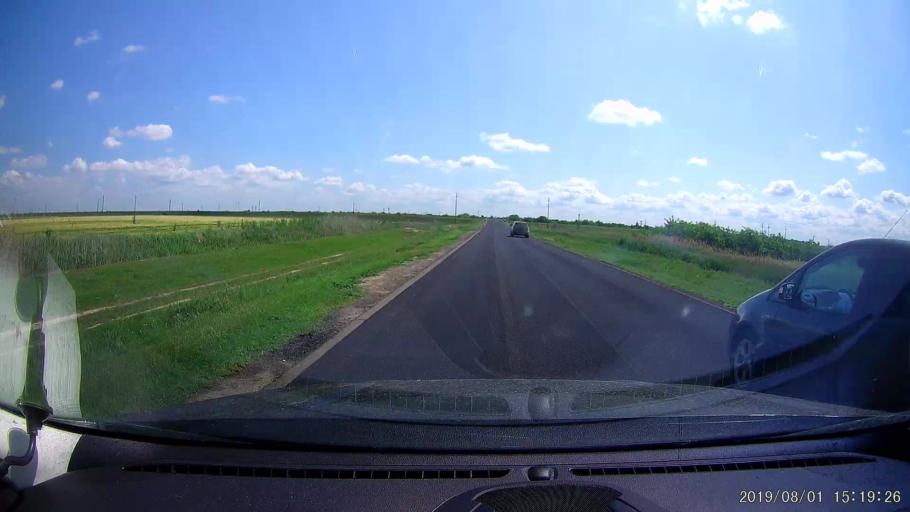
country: RO
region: Braila
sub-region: Comuna Unirea
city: Unirea
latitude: 45.0894
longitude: 27.8126
